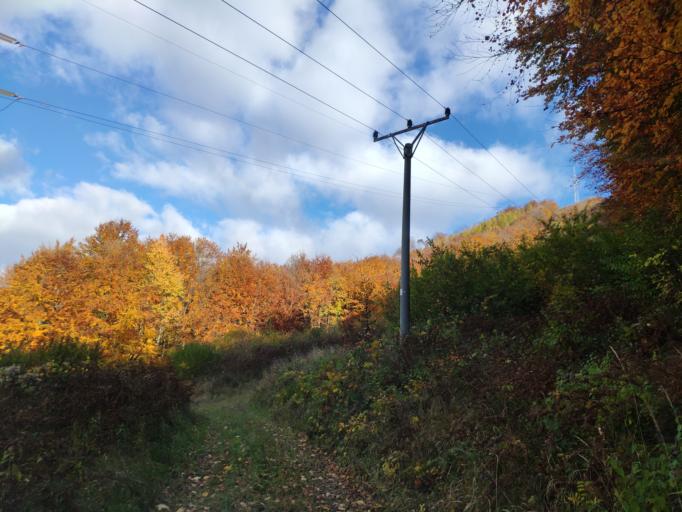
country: SK
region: Presovsky
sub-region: Okres Presov
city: Presov
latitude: 48.8529
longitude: 21.1860
